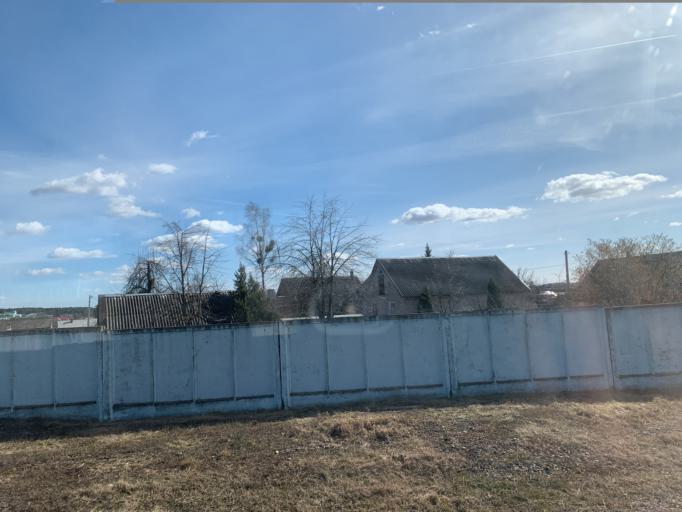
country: BY
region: Minsk
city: Stowbtsy
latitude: 53.4769
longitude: 26.7457
